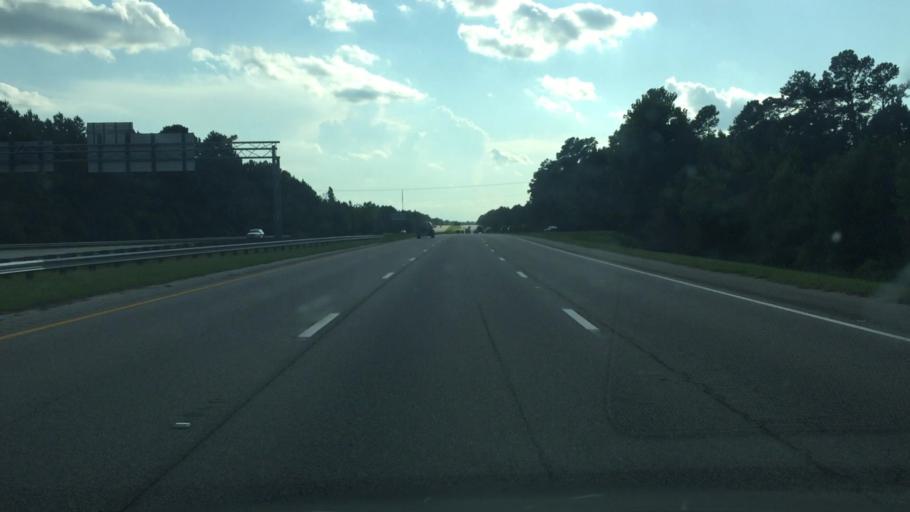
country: US
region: South Carolina
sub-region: Horry County
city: Myrtle Beach
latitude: 33.7529
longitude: -78.8575
